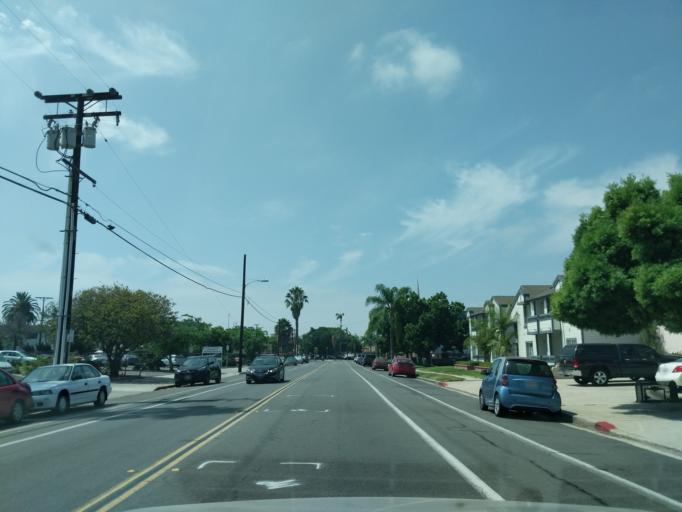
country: US
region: California
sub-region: San Diego County
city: San Diego
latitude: 32.7509
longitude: -117.1496
